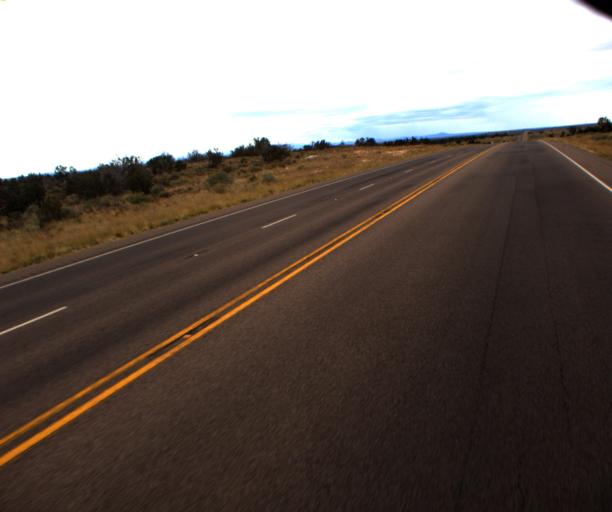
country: US
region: Arizona
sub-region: Navajo County
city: Snowflake
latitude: 34.6317
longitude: -110.0944
